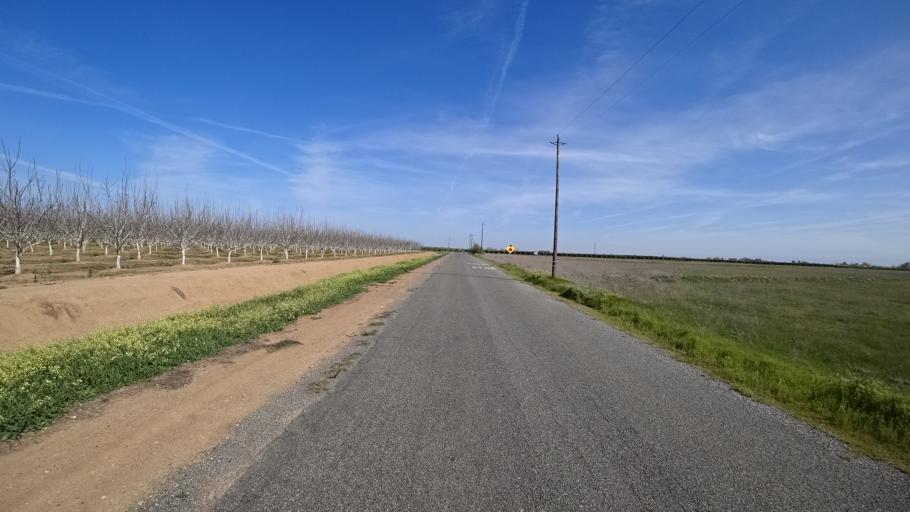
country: US
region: California
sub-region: Glenn County
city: Willows
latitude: 39.6222
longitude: -122.2130
